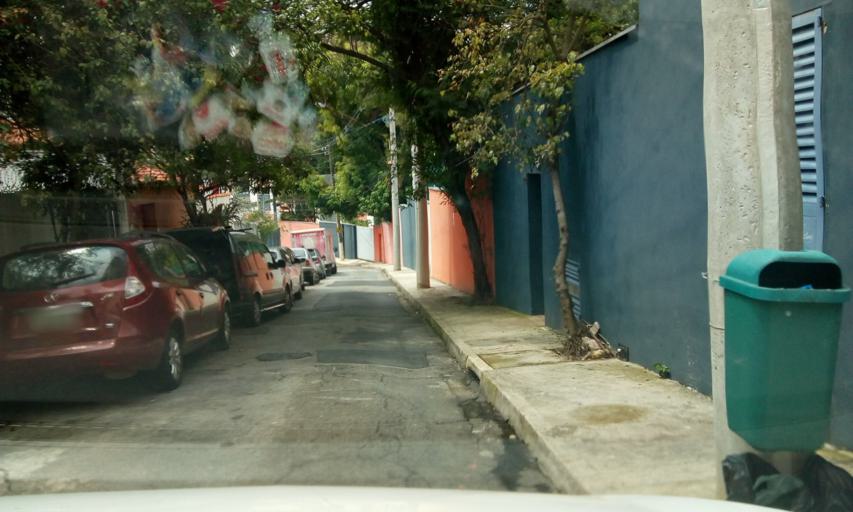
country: BR
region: Sao Paulo
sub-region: Sao Paulo
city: Sao Paulo
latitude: -23.5718
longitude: -46.6283
